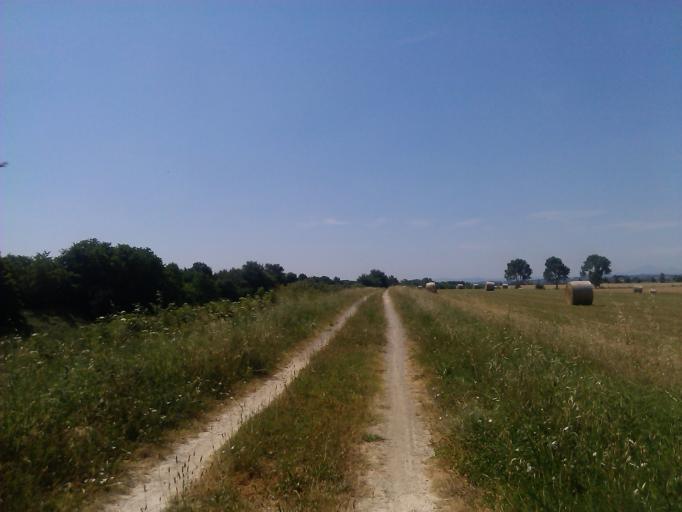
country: IT
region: Tuscany
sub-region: Province of Arezzo
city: Cesa
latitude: 43.3624
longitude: 11.8264
